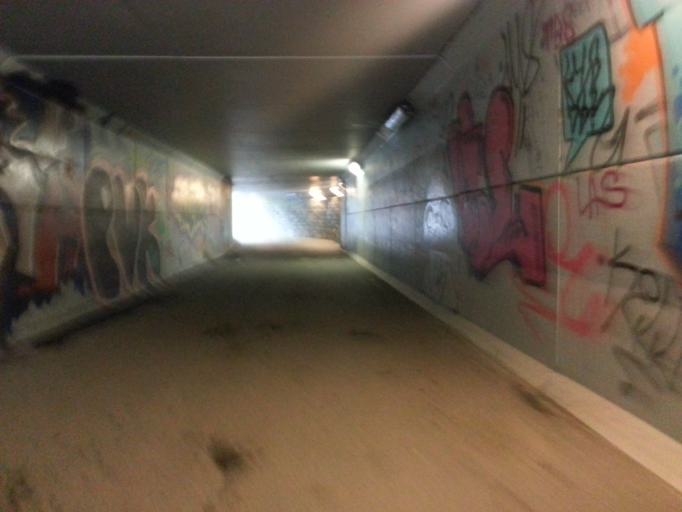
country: NO
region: Sor-Trondelag
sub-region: Trondheim
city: Trondheim
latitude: 63.4280
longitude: 10.3676
